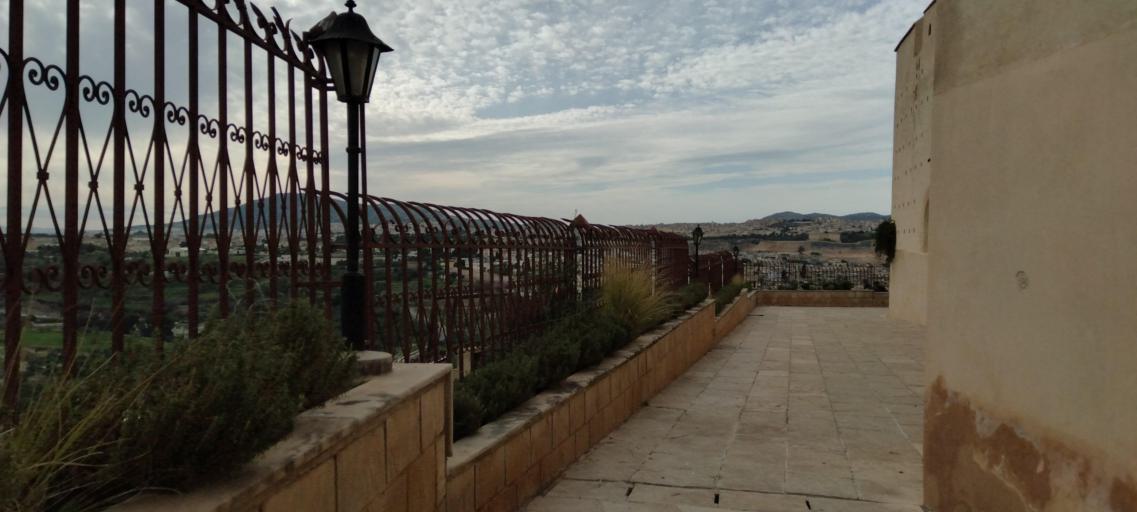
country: MA
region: Fes-Boulemane
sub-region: Fes
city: Fes
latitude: 34.0540
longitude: -4.9703
